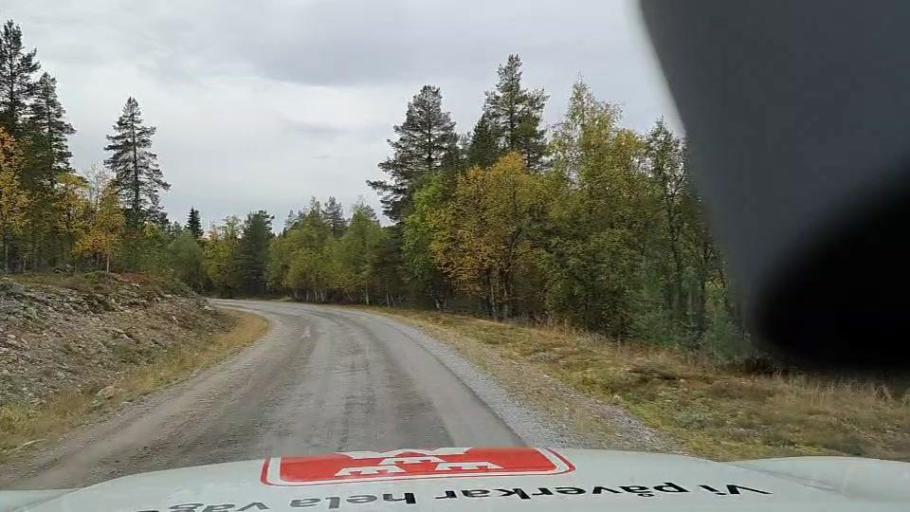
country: NO
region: Hedmark
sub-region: Engerdal
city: Engerdal
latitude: 62.0784
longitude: 12.7454
